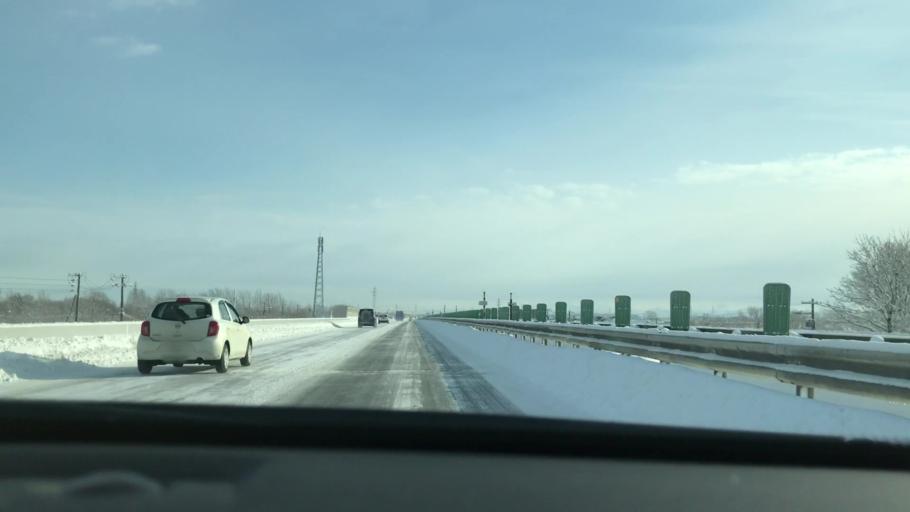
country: JP
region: Hokkaido
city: Ebetsu
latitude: 43.0885
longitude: 141.4550
